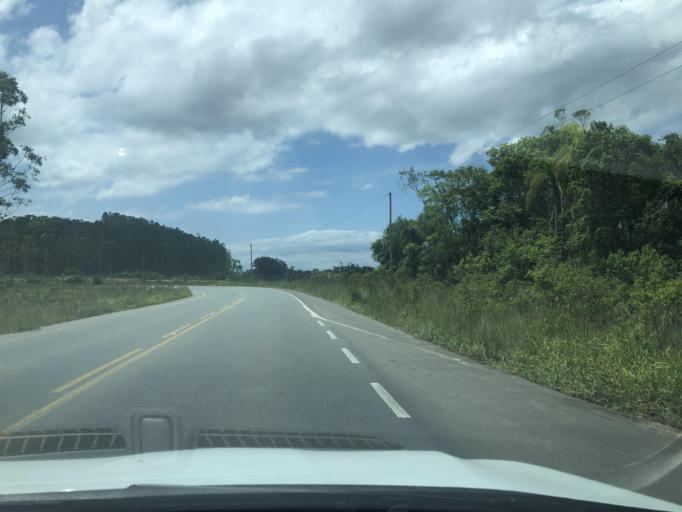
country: BR
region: Santa Catarina
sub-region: Joinville
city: Joinville
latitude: -26.3934
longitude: -48.7656
